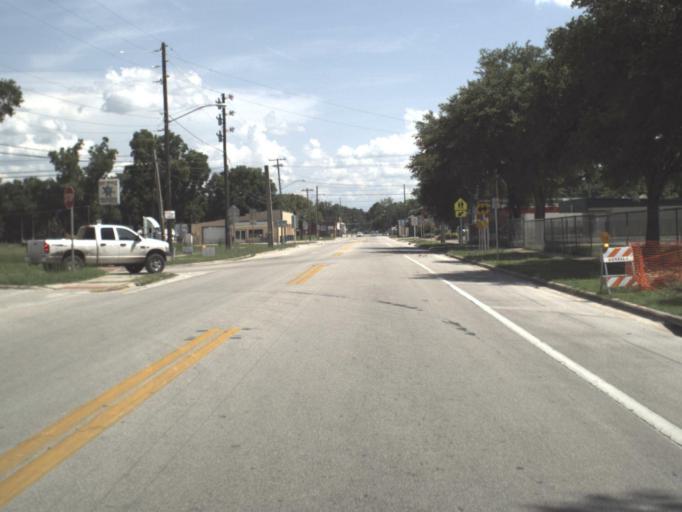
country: US
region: Florida
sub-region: Gilchrist County
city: Trenton
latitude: 29.6189
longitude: -82.8184
